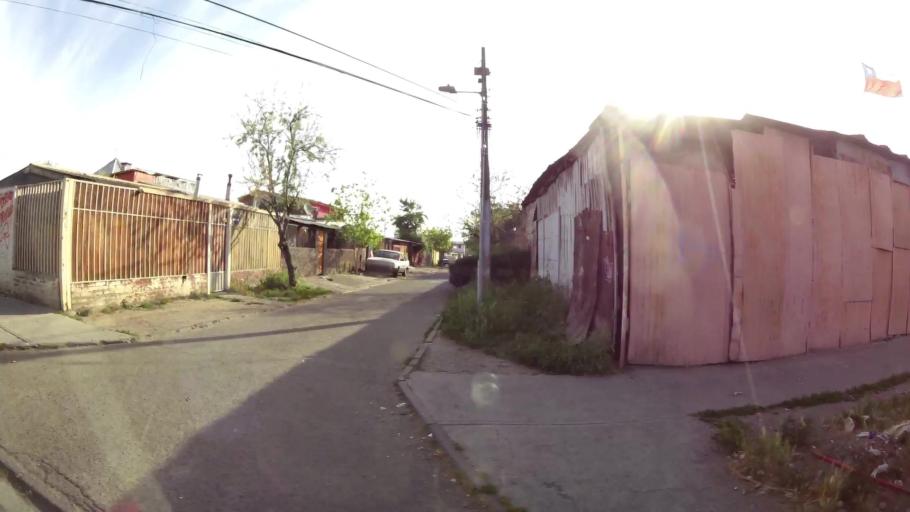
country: CL
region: Santiago Metropolitan
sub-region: Provincia de Cordillera
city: Puente Alto
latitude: -33.6159
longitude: -70.5693
